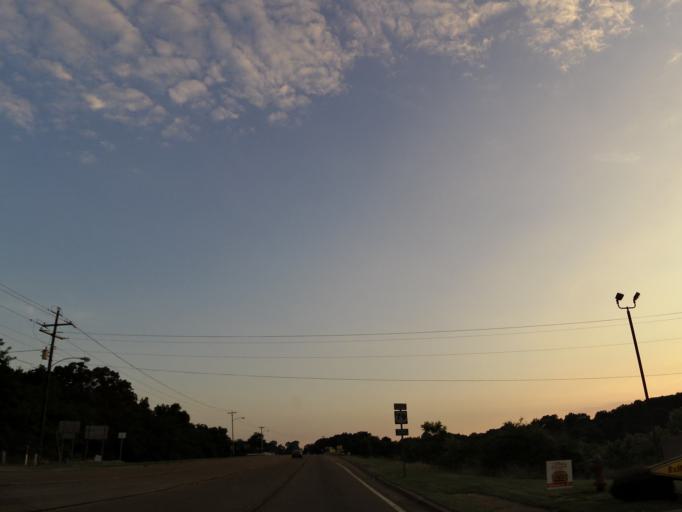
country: US
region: Tennessee
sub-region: Henry County
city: Paris
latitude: 36.2917
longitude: -88.3173
